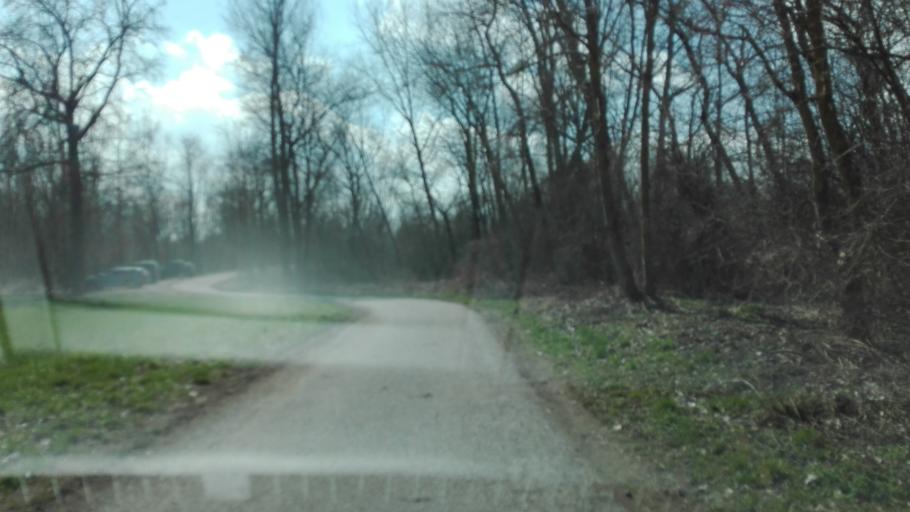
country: AT
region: Upper Austria
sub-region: Politischer Bezirk Urfahr-Umgebung
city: Feldkirchen an der Donau
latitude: 48.3308
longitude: 14.0464
